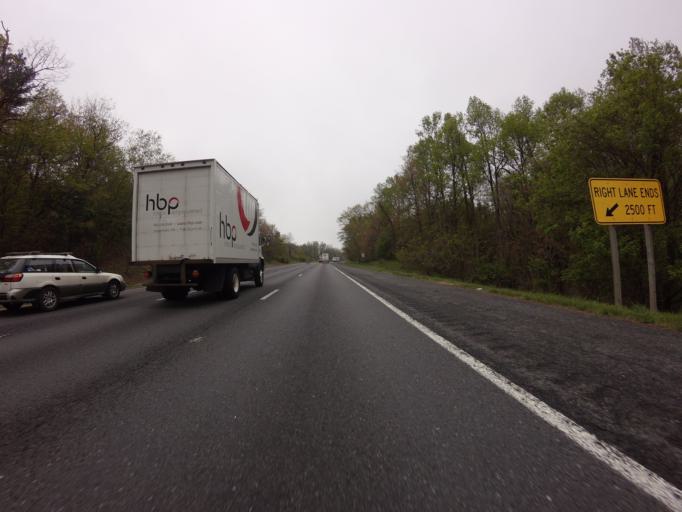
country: US
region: Maryland
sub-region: Frederick County
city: Myersville
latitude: 39.5316
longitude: -77.6043
